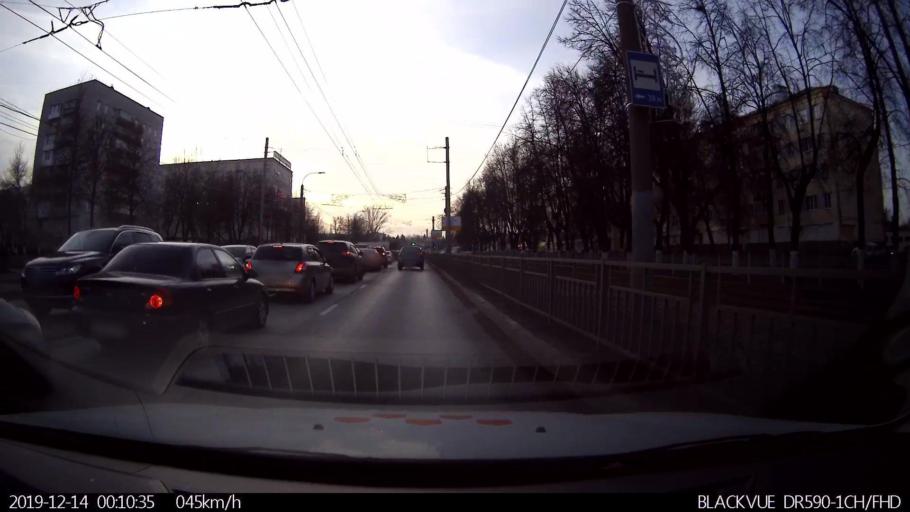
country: RU
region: Nizjnij Novgorod
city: Gorbatovka
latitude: 56.2436
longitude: 43.8682
